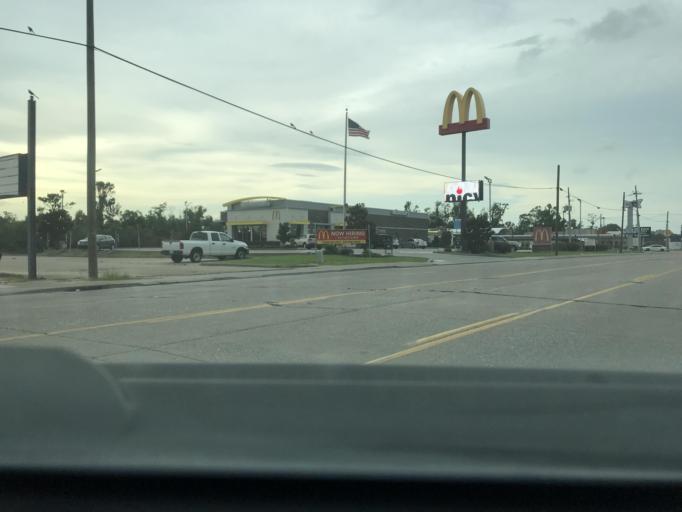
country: US
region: Louisiana
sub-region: Calcasieu Parish
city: Westlake
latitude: 30.2535
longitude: -93.2581
